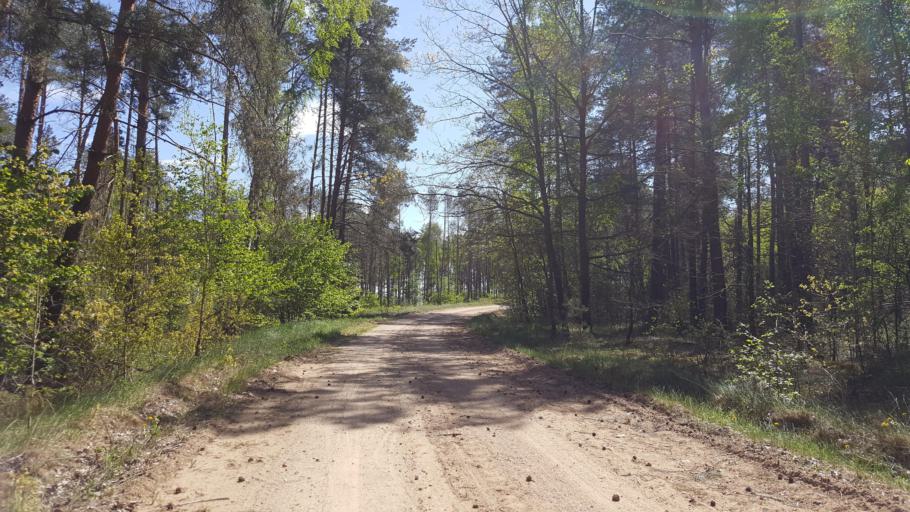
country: BY
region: Brest
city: Zhabinka
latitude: 52.3778
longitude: 24.0246
